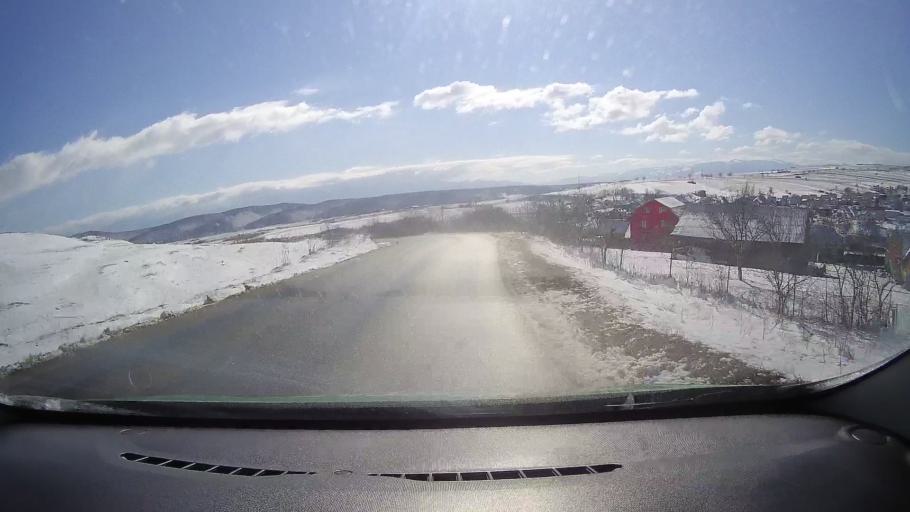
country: RO
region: Sibiu
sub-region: Comuna Rosia
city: Rosia
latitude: 45.8033
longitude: 24.2918
